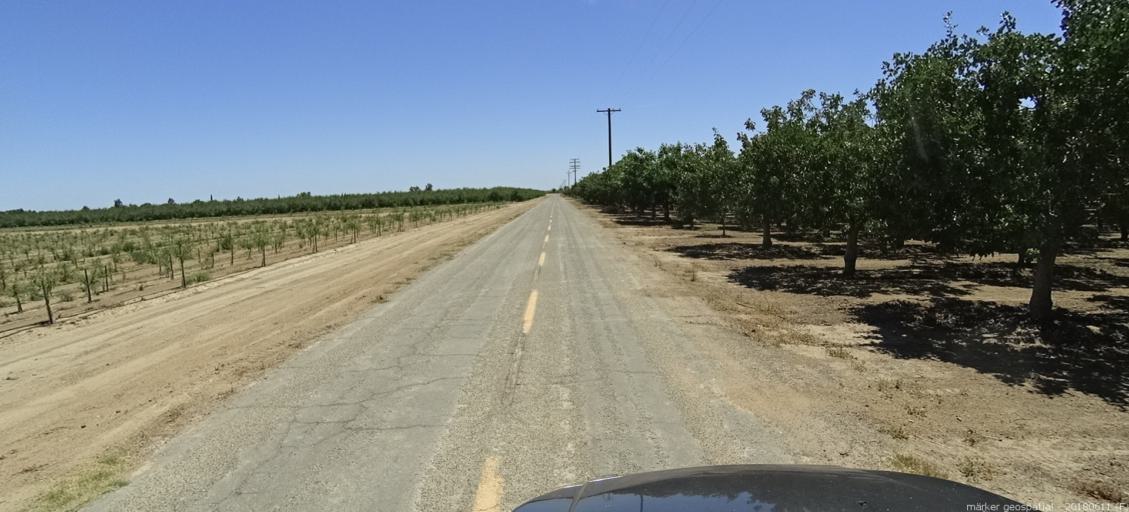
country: US
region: California
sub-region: Madera County
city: Fairmead
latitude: 37.0234
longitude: -120.2114
